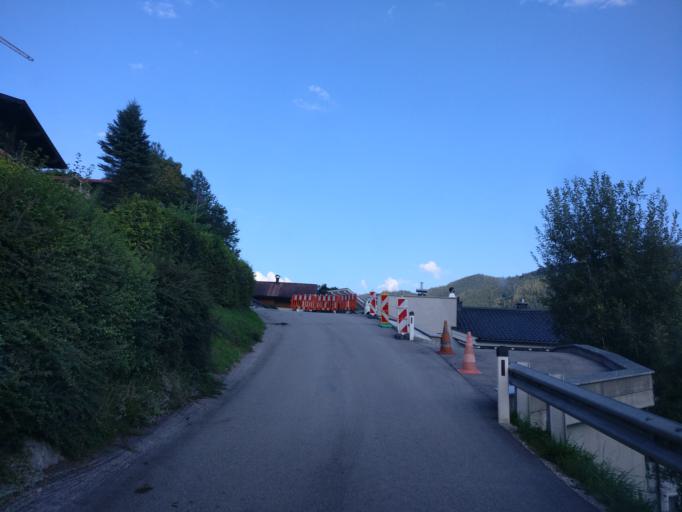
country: AT
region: Salzburg
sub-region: Politischer Bezirk Sankt Johann im Pongau
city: Muhlbach am Hochkonig
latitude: 47.3786
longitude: 13.1276
